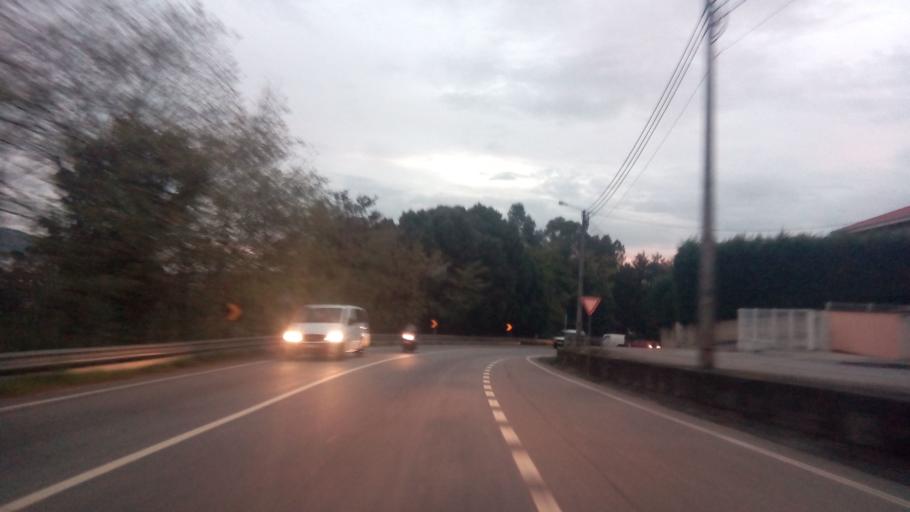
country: PT
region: Porto
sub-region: Paredes
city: Gandra
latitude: 41.1901
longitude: -8.4357
